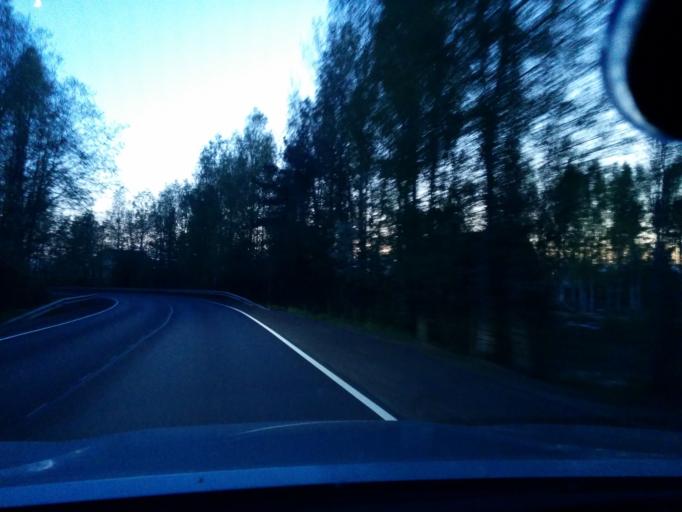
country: RU
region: Leningrad
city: Luppolovo
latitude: 60.1795
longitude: 30.3691
